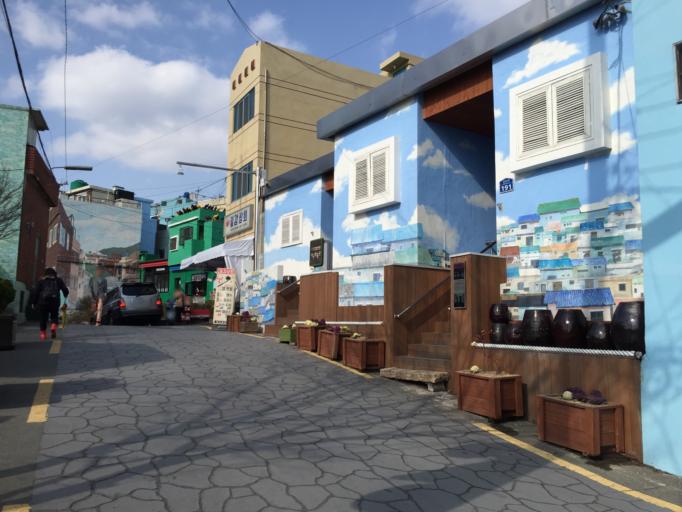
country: KR
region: Busan
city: Busan
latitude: 35.0978
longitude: 129.0103
